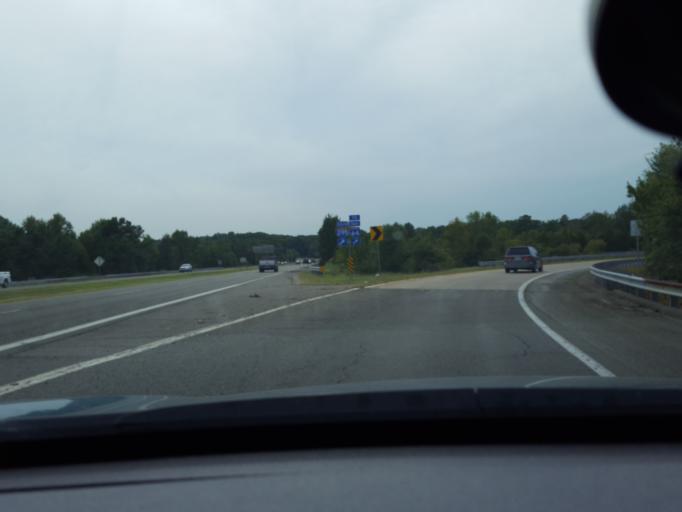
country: US
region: Virginia
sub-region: Henrico County
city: Chamberlayne
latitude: 37.6444
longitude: -77.4150
